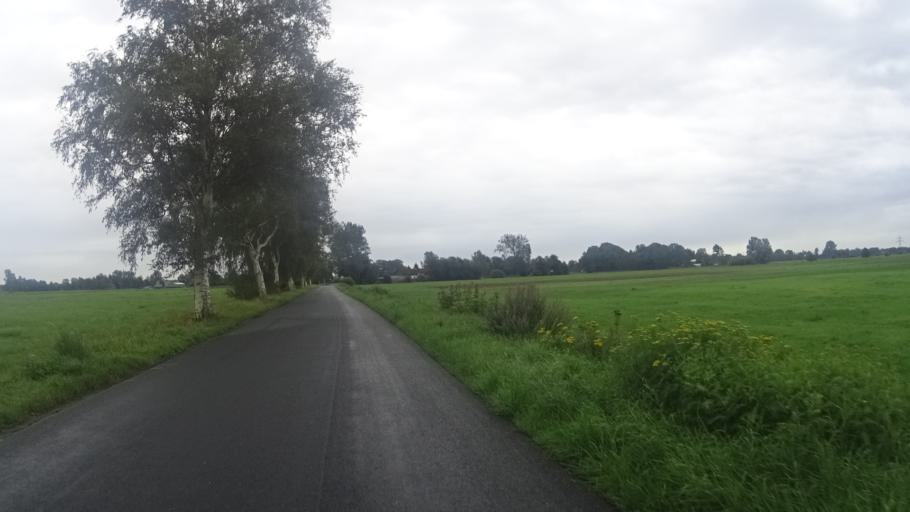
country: DE
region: Schleswig-Holstein
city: Raa-Besenbek
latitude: 53.7908
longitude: 9.5895
